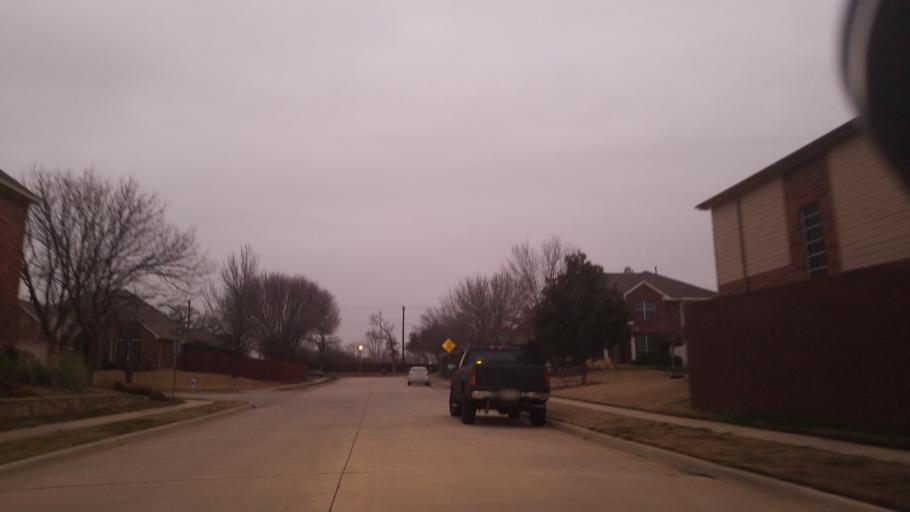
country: US
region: Texas
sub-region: Denton County
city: Corinth
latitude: 33.1615
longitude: -97.0915
